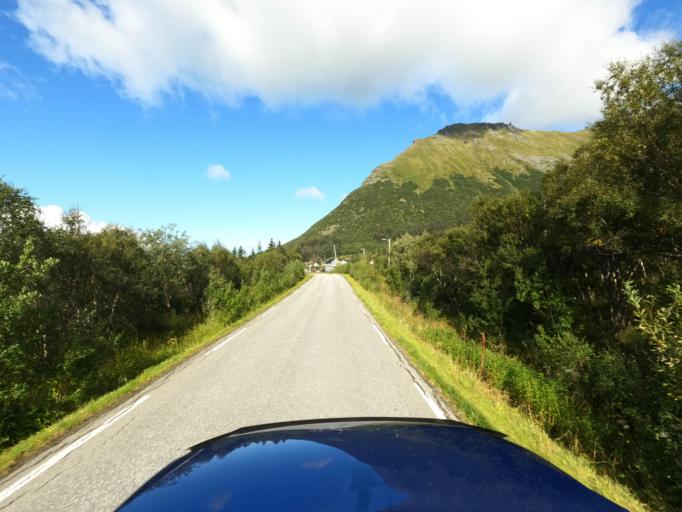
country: NO
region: Nordland
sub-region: Vagan
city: Kabelvag
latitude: 68.2838
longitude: 14.3485
